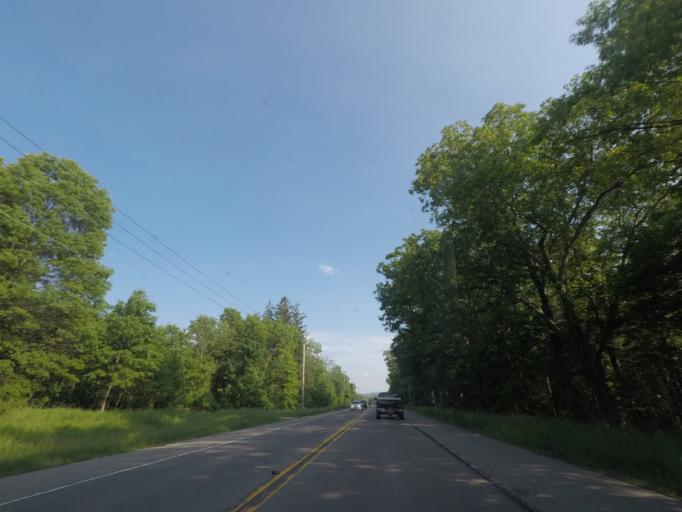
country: US
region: New York
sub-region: Orange County
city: Beaverdam Lake-Salisbury Mills
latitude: 41.4858
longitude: -74.1319
